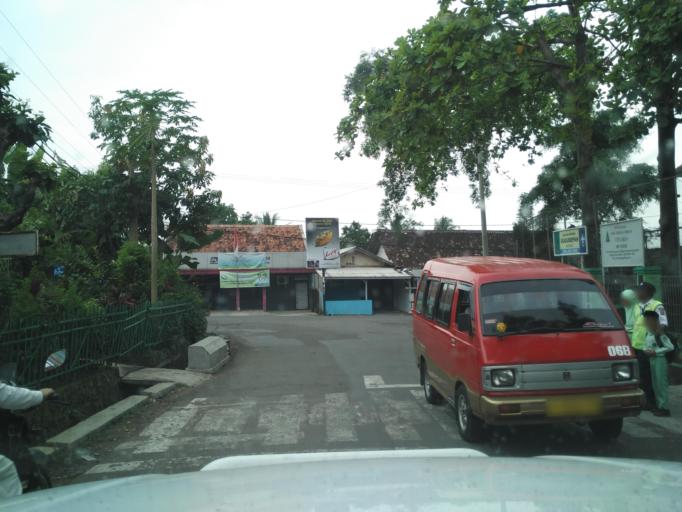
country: ID
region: West Java
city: Ciranjang-hilir
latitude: -6.8209
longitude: 107.1736
